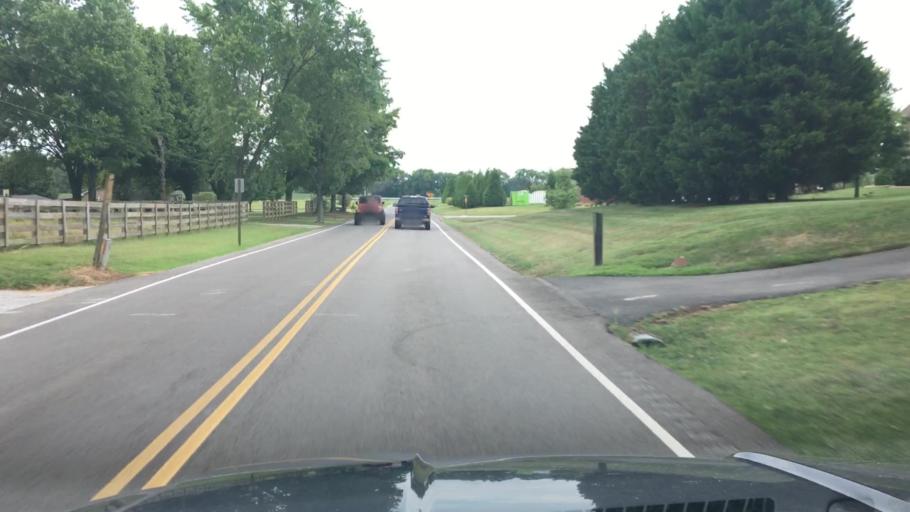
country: US
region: Tennessee
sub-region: Williamson County
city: Thompson's Station
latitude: 35.7925
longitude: -86.8642
